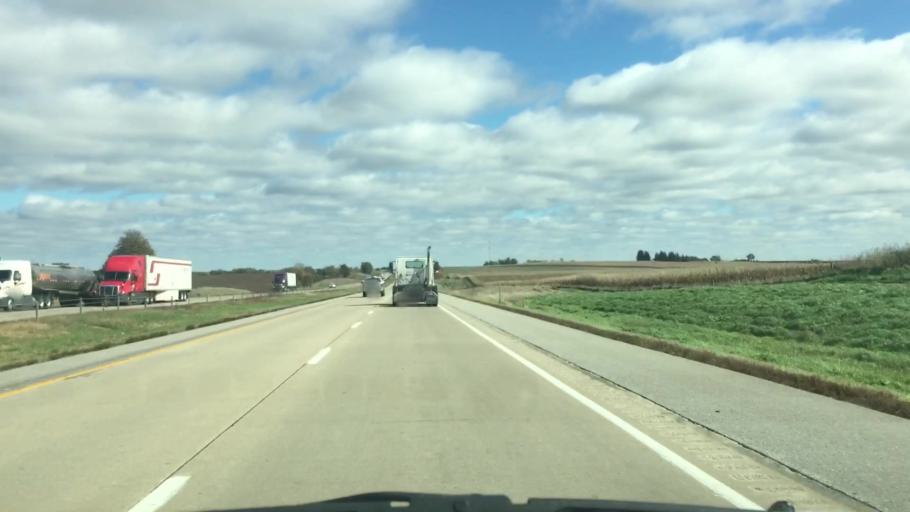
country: US
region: Iowa
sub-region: Poweshiek County
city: Brooklyn
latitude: 41.6942
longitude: -92.4945
